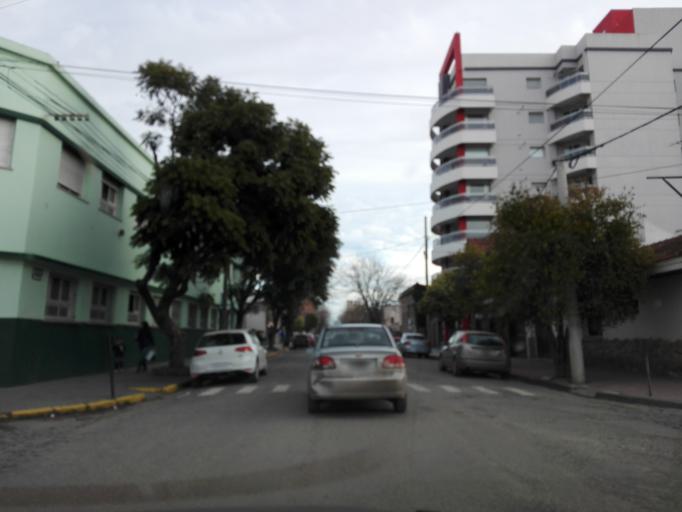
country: AR
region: Buenos Aires
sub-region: Partido de Balcarce
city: Balcarce
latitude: -37.8464
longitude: -58.2515
